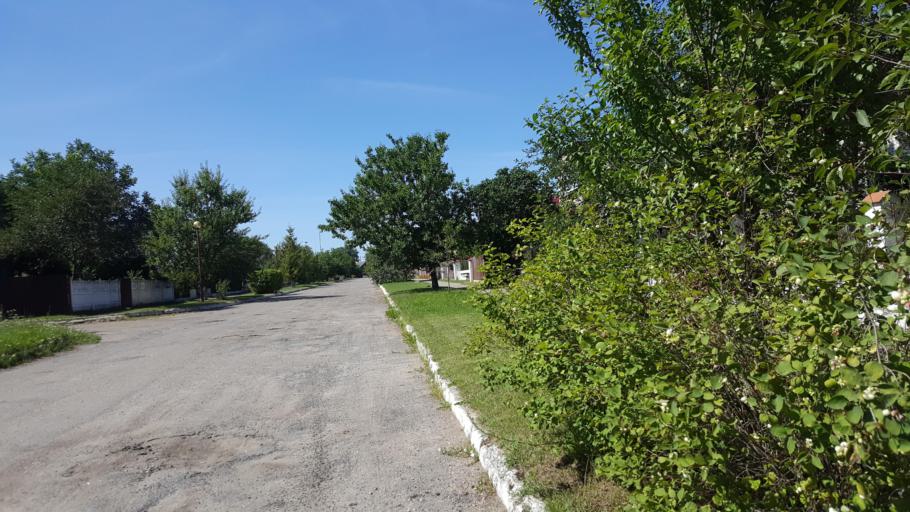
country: BY
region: Brest
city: Charnawchytsy
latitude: 52.2639
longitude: 23.5947
